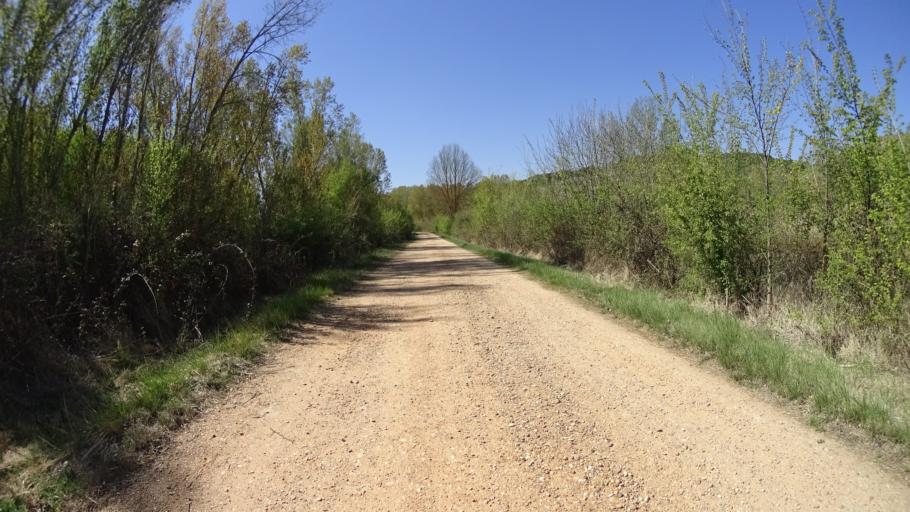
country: ES
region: Castille and Leon
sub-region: Provincia de Palencia
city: Villamuriel de Cerrato
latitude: 41.9190
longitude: -4.5265
